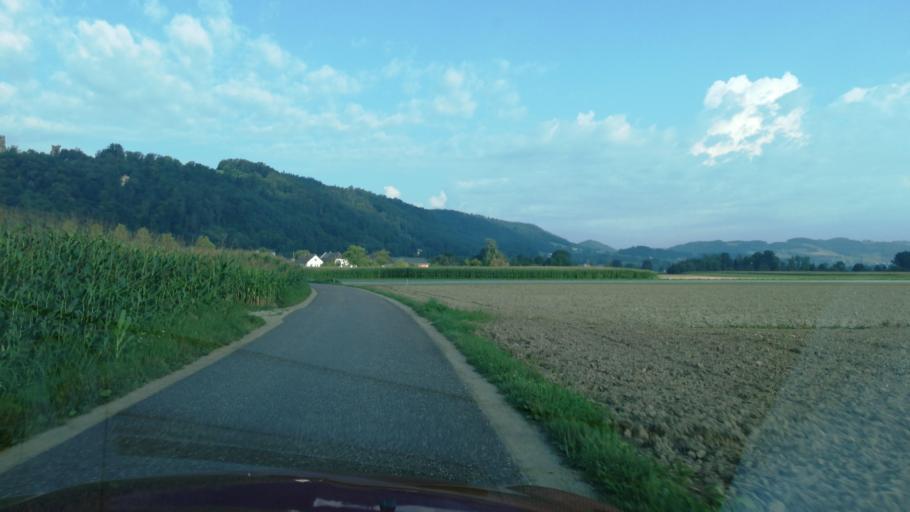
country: AT
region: Upper Austria
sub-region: Politischer Bezirk Urfahr-Umgebung
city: Feldkirchen an der Donau
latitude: 48.3406
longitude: 13.9903
